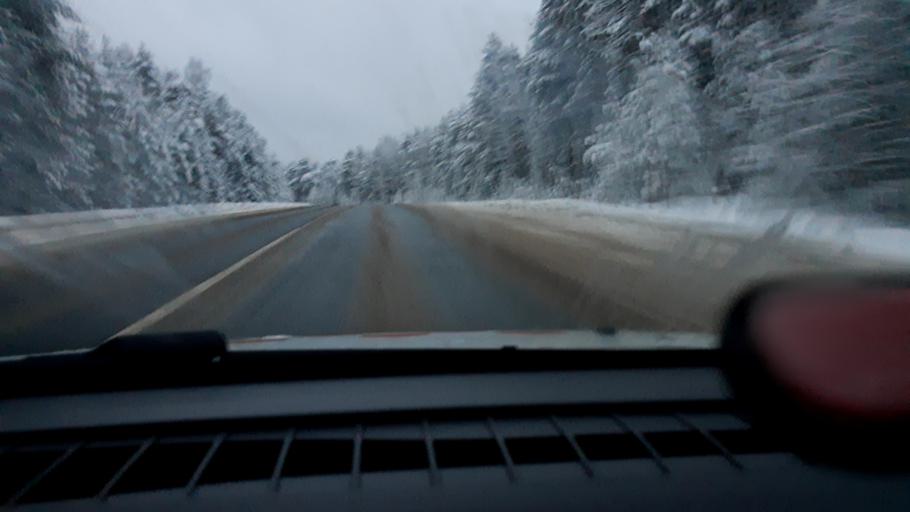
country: RU
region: Nizjnij Novgorod
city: Krasnyye Baki
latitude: 57.1761
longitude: 45.3494
